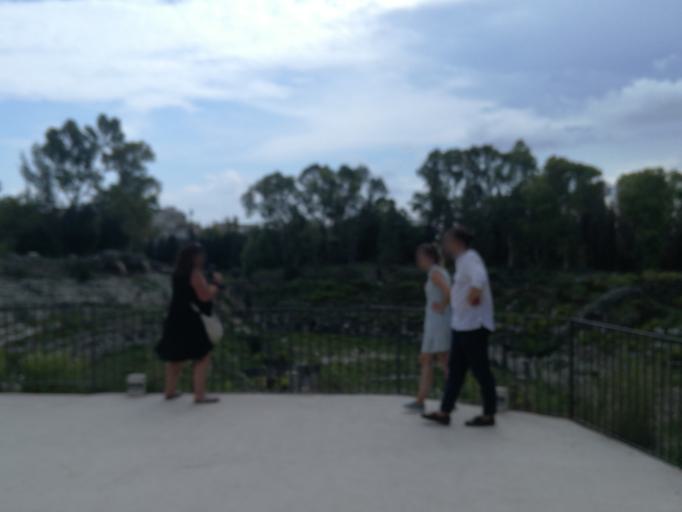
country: IT
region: Sicily
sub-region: Provincia di Siracusa
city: Siracusa
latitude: 37.0748
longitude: 15.2786
